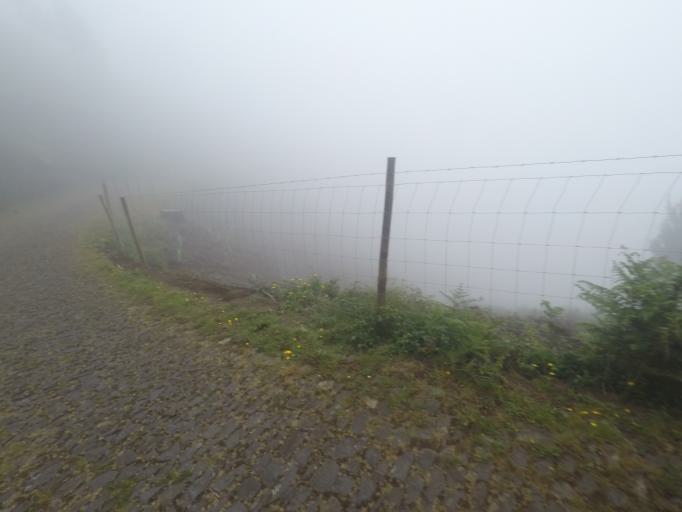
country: PT
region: Madeira
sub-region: Calheta
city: Arco da Calheta
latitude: 32.7320
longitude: -17.0969
